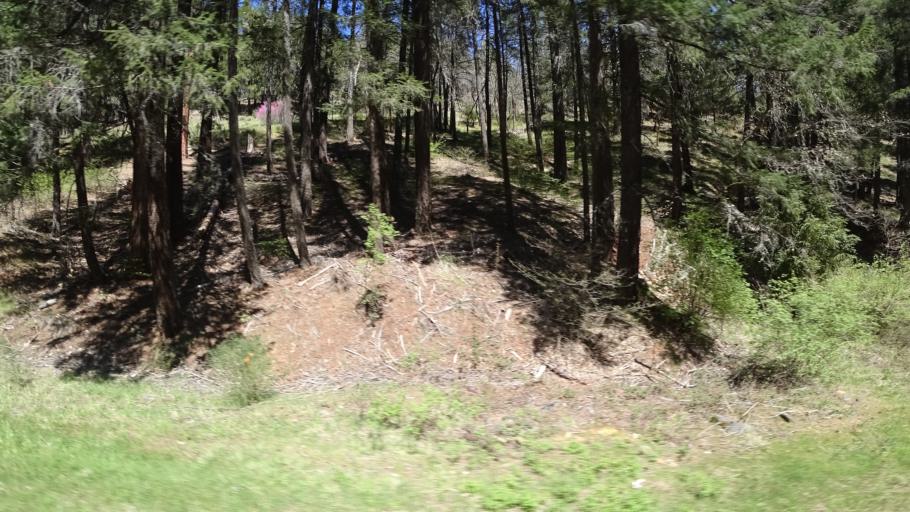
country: US
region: California
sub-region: Trinity County
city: Weaverville
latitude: 40.7655
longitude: -122.8890
